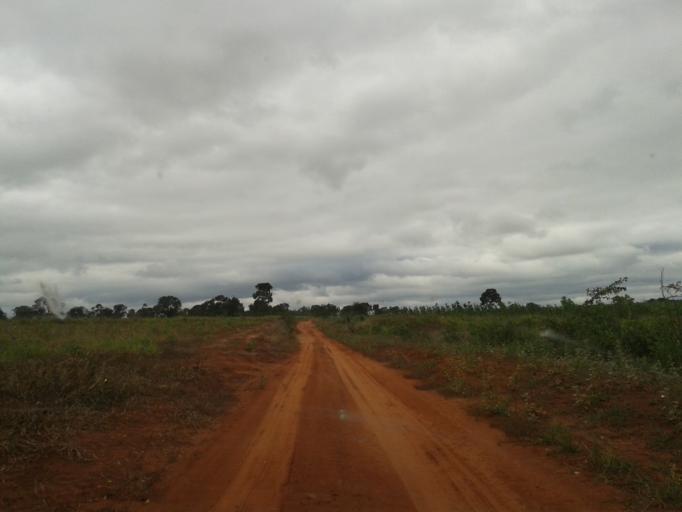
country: BR
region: Minas Gerais
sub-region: Campina Verde
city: Campina Verde
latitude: -19.5124
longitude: -49.6325
